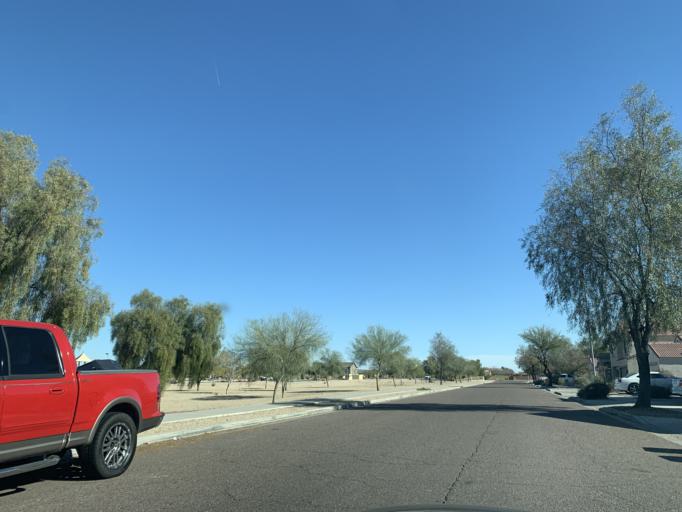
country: US
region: Arizona
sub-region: Maricopa County
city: Laveen
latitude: 33.3958
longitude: -112.1275
